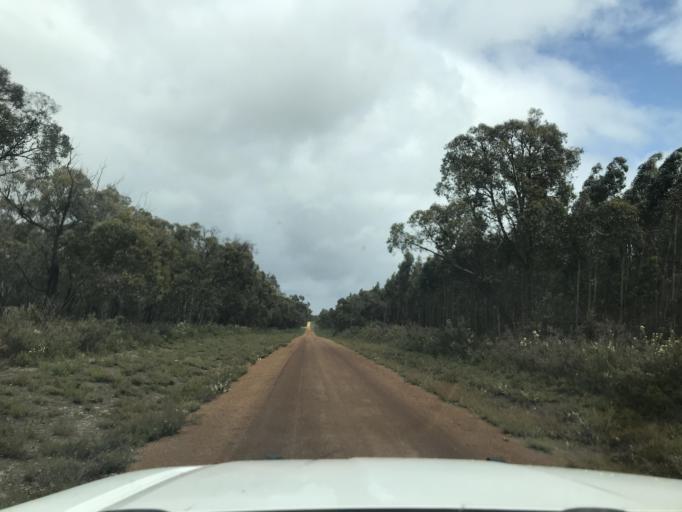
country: AU
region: South Australia
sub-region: Wattle Range
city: Penola
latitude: -37.2936
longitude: 141.3014
